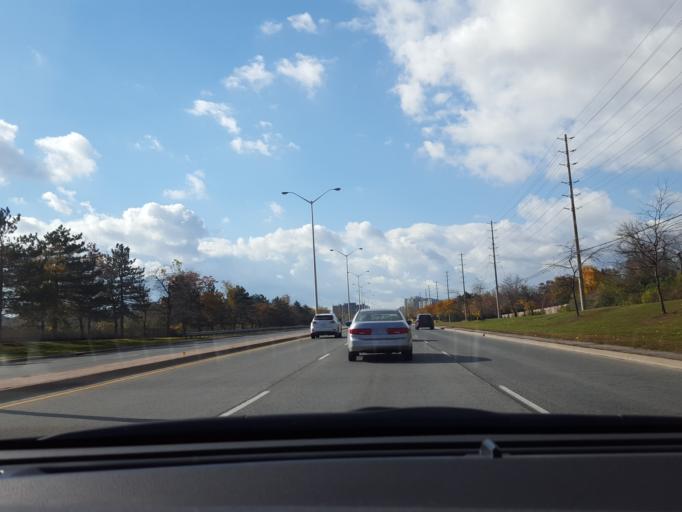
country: CA
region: Ontario
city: Brampton
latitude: 43.7320
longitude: -79.7092
